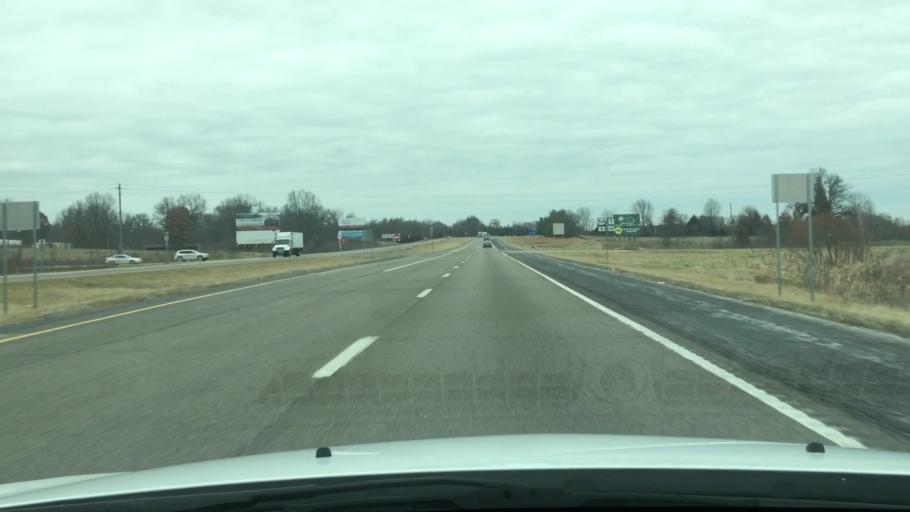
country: US
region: Missouri
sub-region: Callaway County
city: Fulton
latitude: 39.0024
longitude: -91.8933
